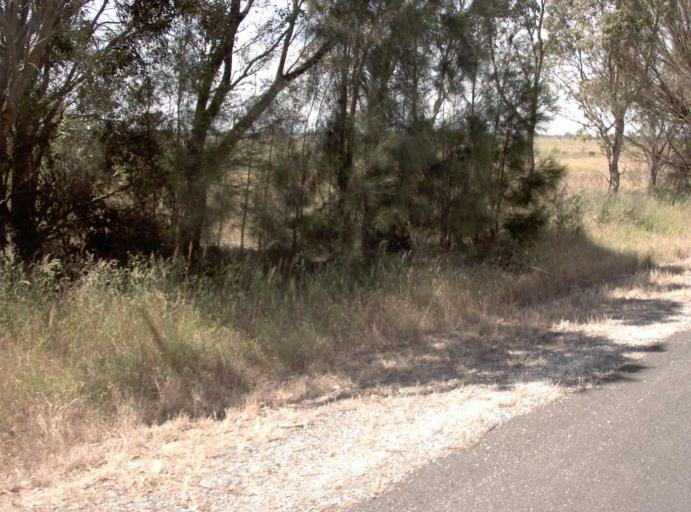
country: AU
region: Victoria
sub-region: Wellington
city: Heyfield
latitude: -38.1141
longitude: 146.8767
